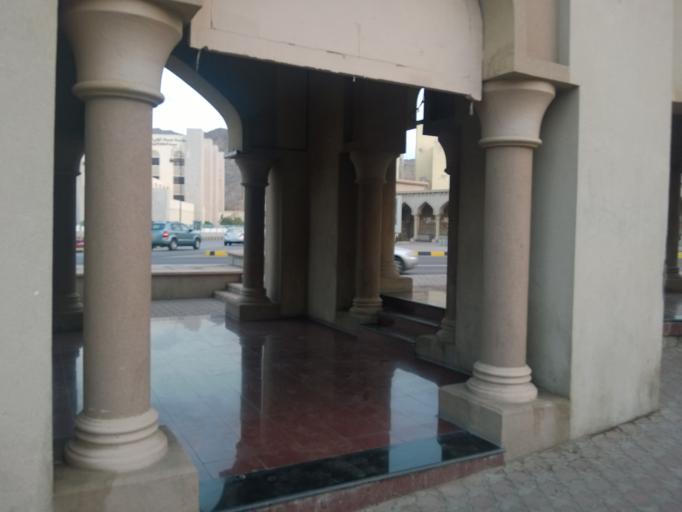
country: OM
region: Muhafazat Masqat
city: Muscat
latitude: 23.6231
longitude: 58.5593
